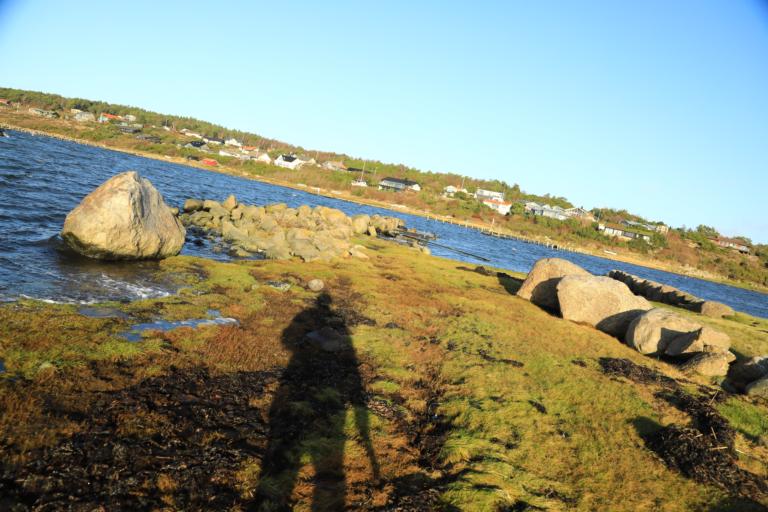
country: SE
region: Halland
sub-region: Varbergs Kommun
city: Varberg
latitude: 57.1662
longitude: 12.2114
